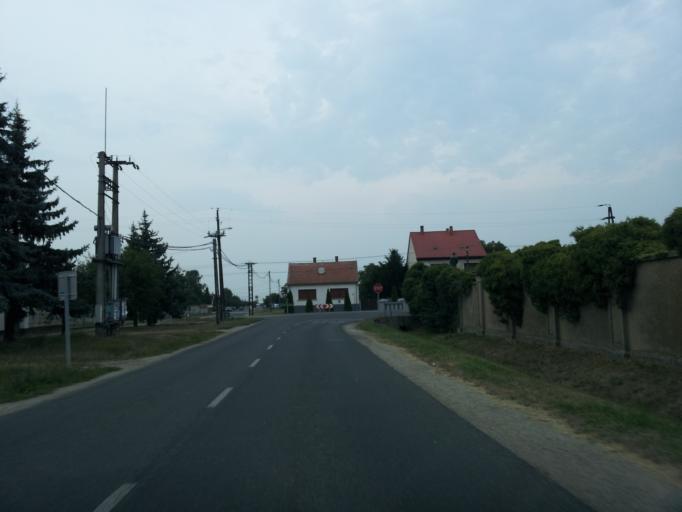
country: HU
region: Vas
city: Sarvar
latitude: 47.2086
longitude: 16.8953
